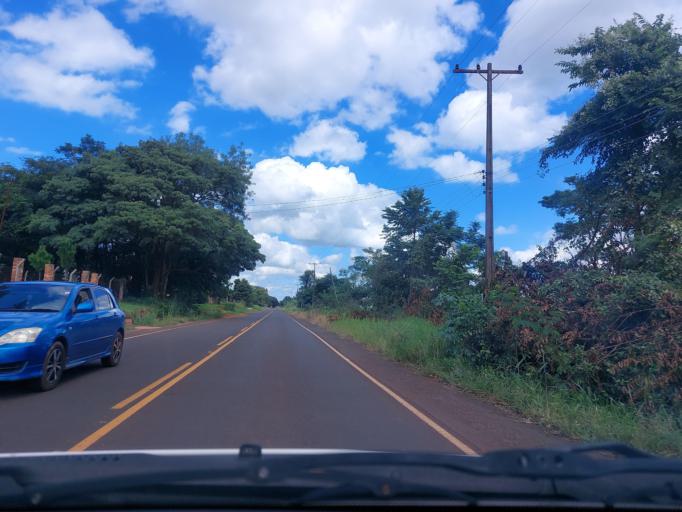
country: PY
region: San Pedro
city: Guayaybi
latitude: -24.5889
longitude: -56.5196
